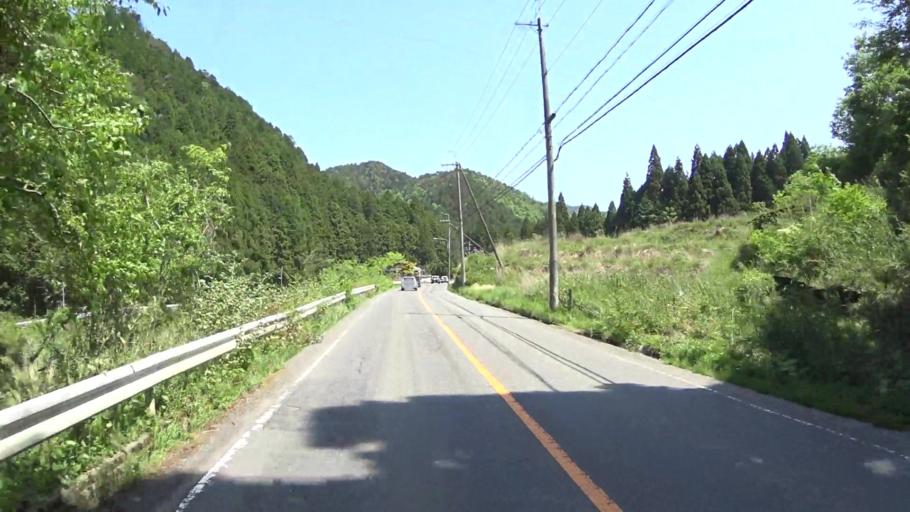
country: JP
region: Shiga Prefecture
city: Kitahama
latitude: 35.1378
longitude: 135.8355
